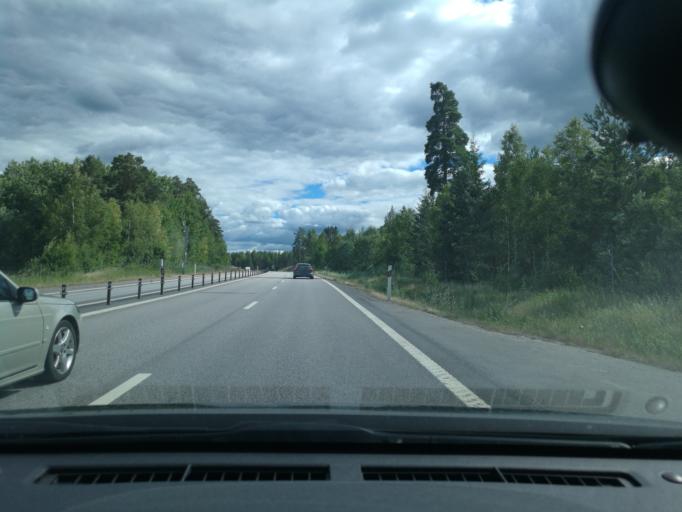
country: SE
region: OEstergoetland
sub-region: Soderkopings Kommun
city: Soederkoeping
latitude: 58.4460
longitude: 16.3663
